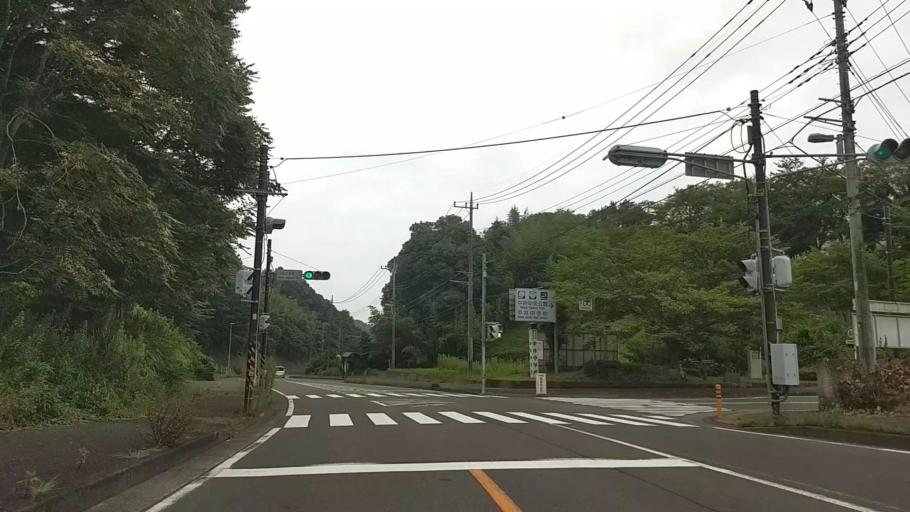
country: JP
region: Kanagawa
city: Hadano
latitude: 35.3352
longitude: 139.2194
